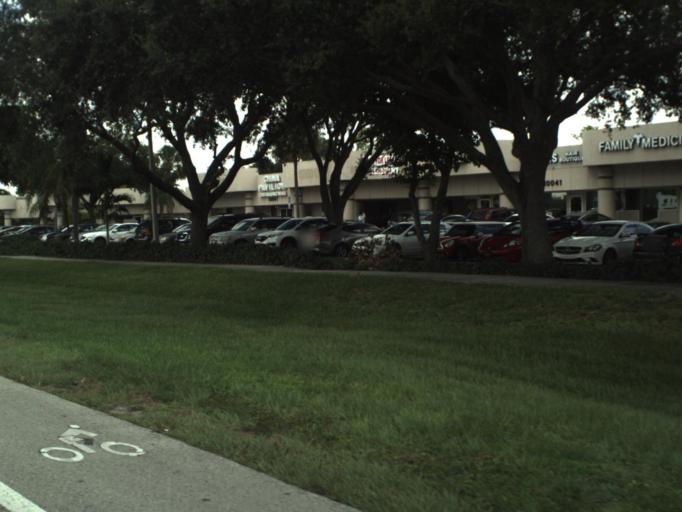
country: US
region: Florida
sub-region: Broward County
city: Cooper City
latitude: 26.0084
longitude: -80.2778
